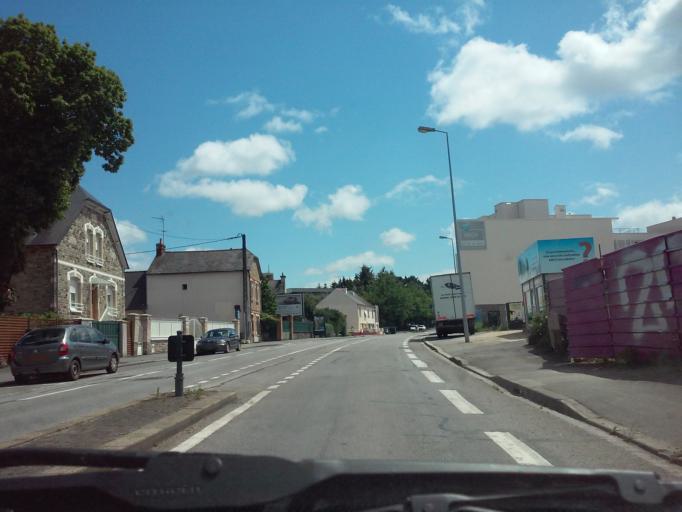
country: FR
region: Brittany
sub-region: Departement d'Ille-et-Vilaine
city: Chantepie
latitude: 48.0989
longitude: -1.6450
